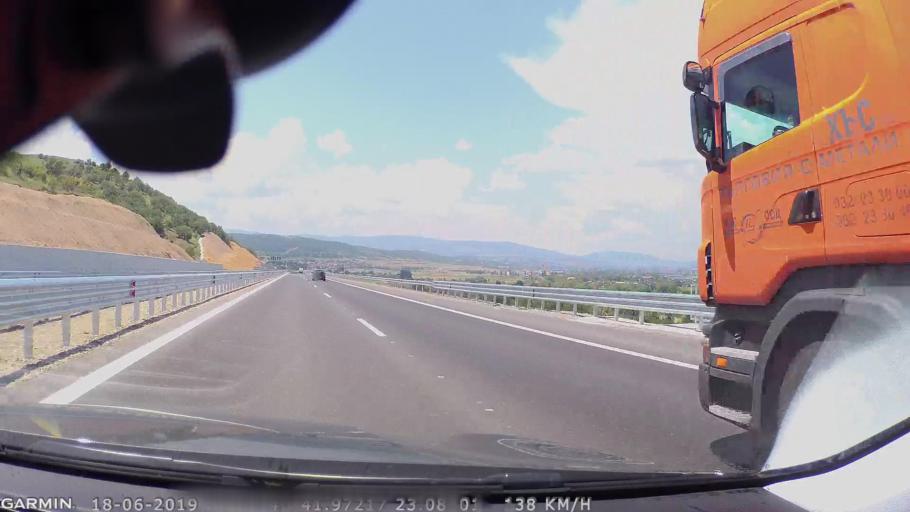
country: BG
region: Blagoevgrad
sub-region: Obshtina Blagoevgrad
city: Blagoevgrad
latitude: 41.9715
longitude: 23.0825
